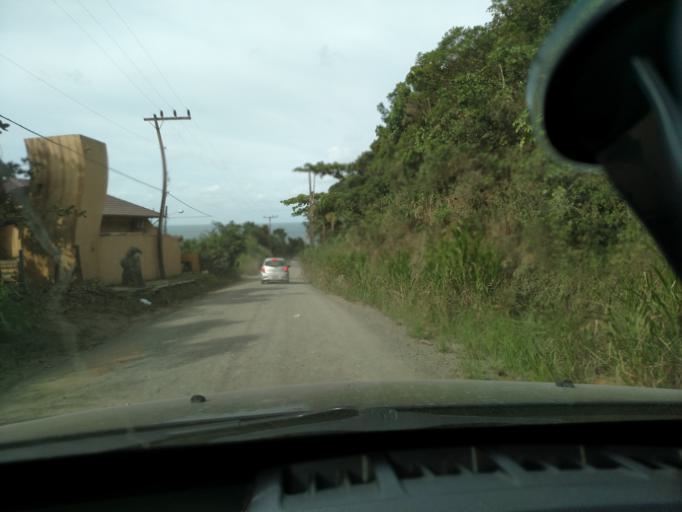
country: BR
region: Santa Catarina
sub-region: Porto Belo
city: Porto Belo
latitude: -27.2052
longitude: -48.4920
